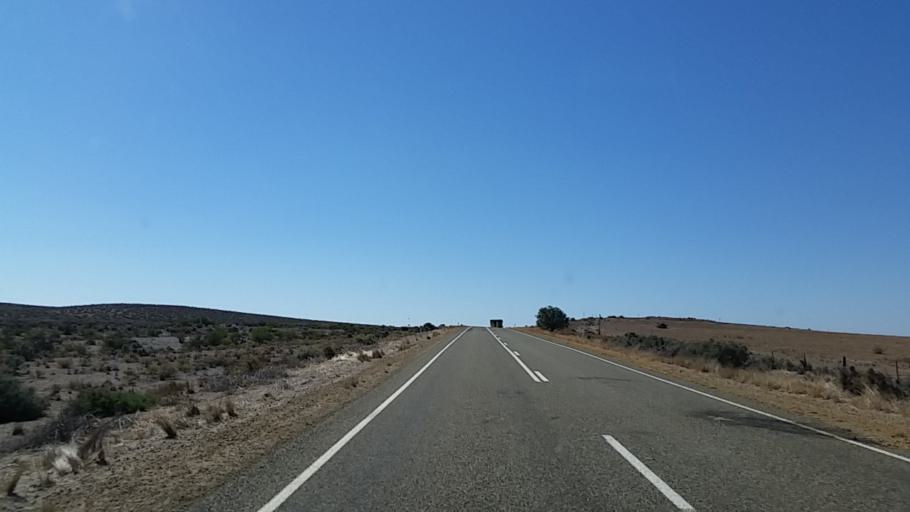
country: AU
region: South Australia
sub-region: Flinders Ranges
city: Quorn
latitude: -32.1892
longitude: 138.5353
